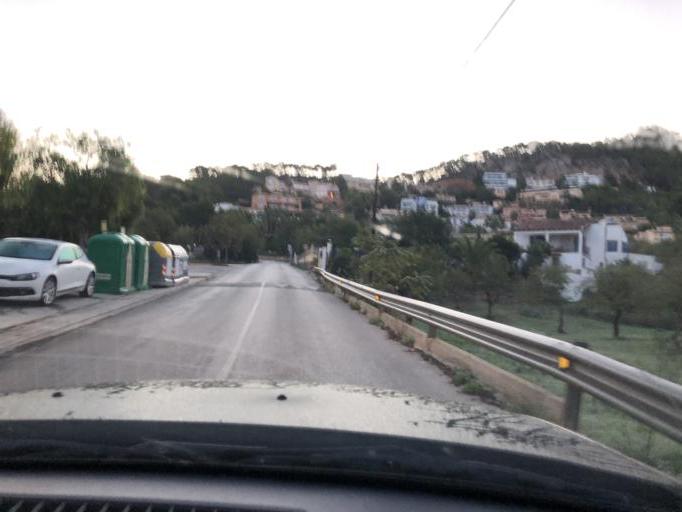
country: ES
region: Balearic Islands
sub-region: Illes Balears
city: Camp de Mar
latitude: 39.5422
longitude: 2.3905
